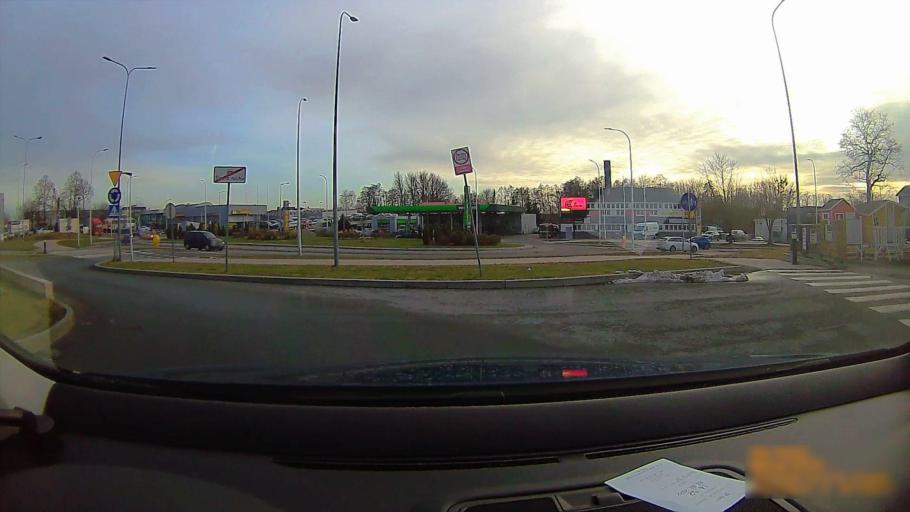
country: PL
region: Greater Poland Voivodeship
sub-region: Konin
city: Konin
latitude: 52.2325
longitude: 18.2314
